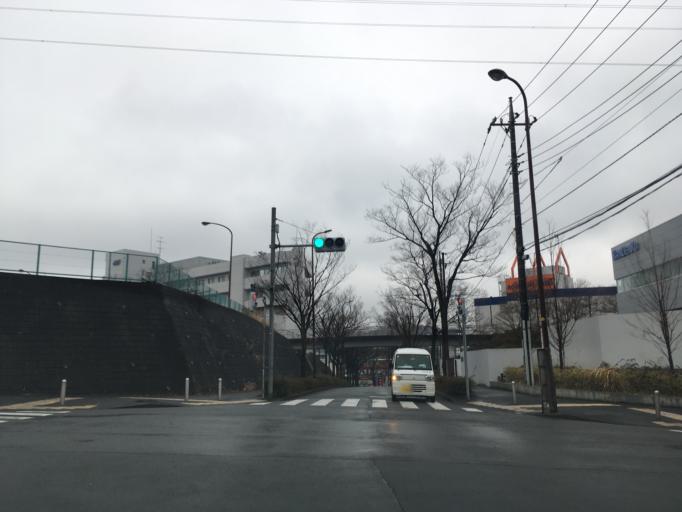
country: JP
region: Tokyo
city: Hino
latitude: 35.6140
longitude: 139.4446
